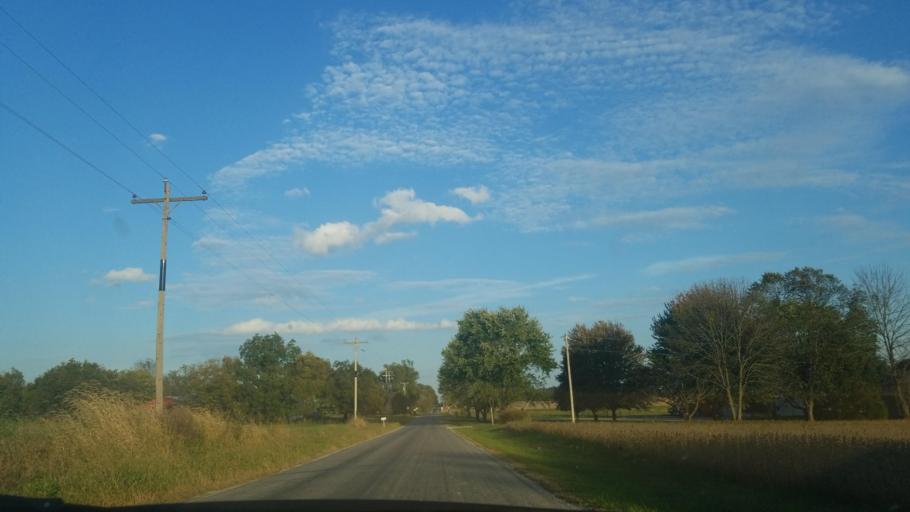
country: US
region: Illinois
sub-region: Saline County
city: Carrier Mills
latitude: 37.8050
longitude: -88.6547
